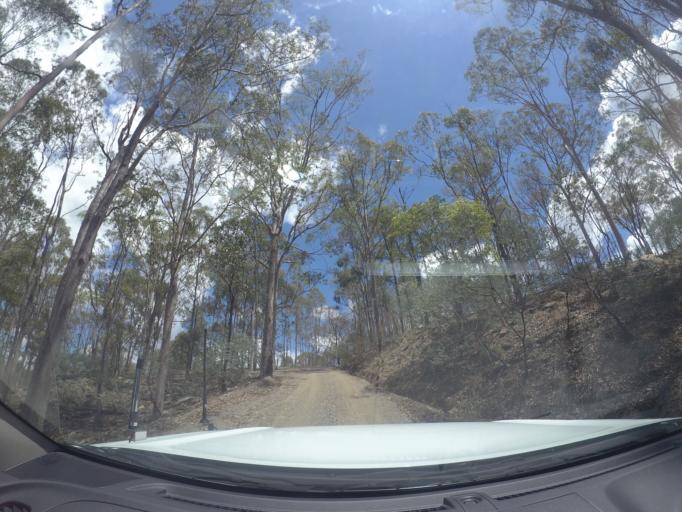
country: AU
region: Queensland
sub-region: Logan
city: Cedar Vale
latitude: -27.9163
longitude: 153.0486
